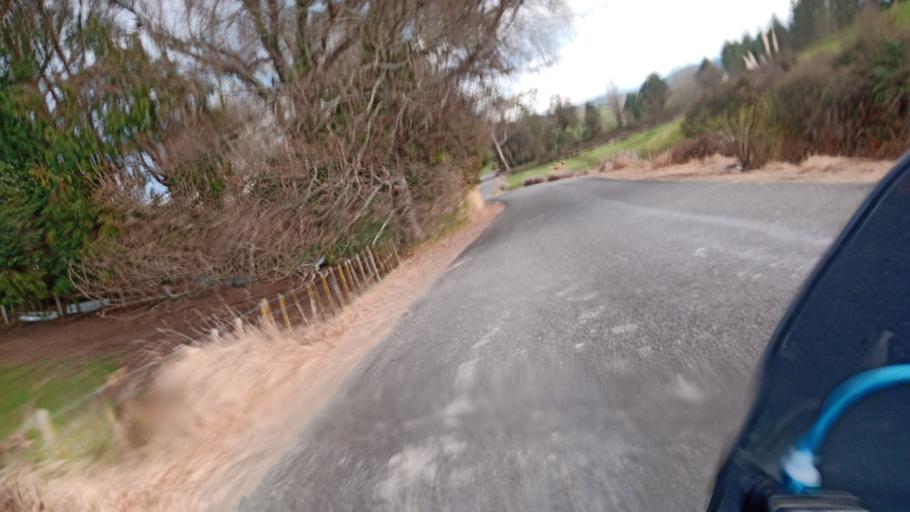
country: NZ
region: Hawke's Bay
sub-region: Wairoa District
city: Wairoa
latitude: -38.9748
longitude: 177.4270
